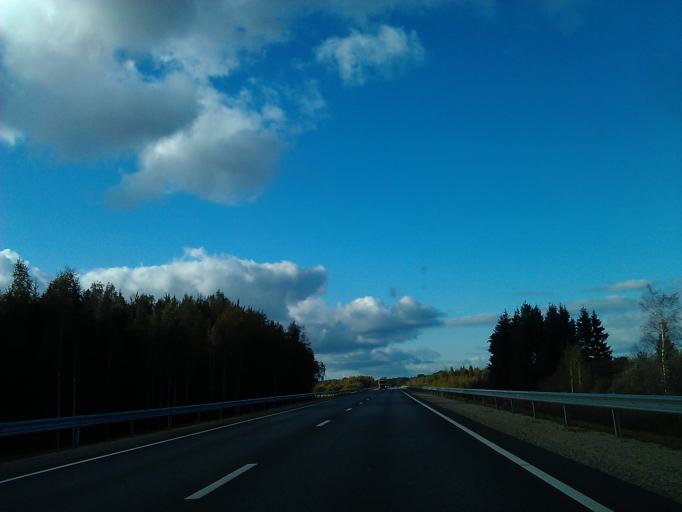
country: LV
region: Skriveri
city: Skriveri
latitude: 56.7487
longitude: 25.1222
